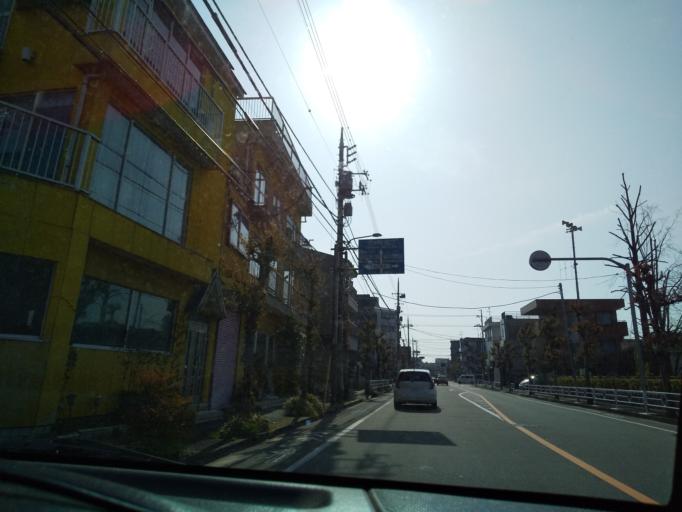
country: JP
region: Tokyo
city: Hino
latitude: 35.6994
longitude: 139.3951
